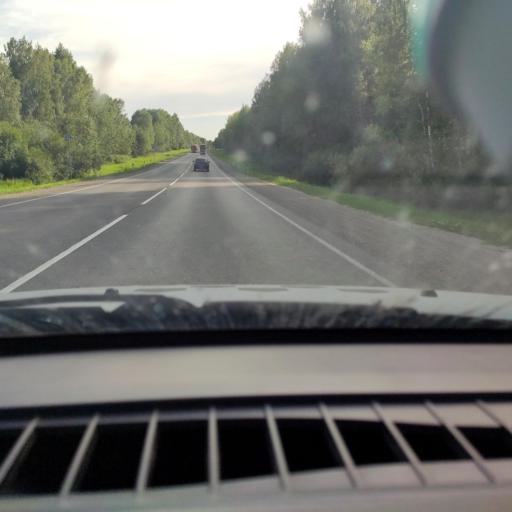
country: RU
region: Kirov
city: Vakhrushi
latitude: 58.6459
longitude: 49.8593
